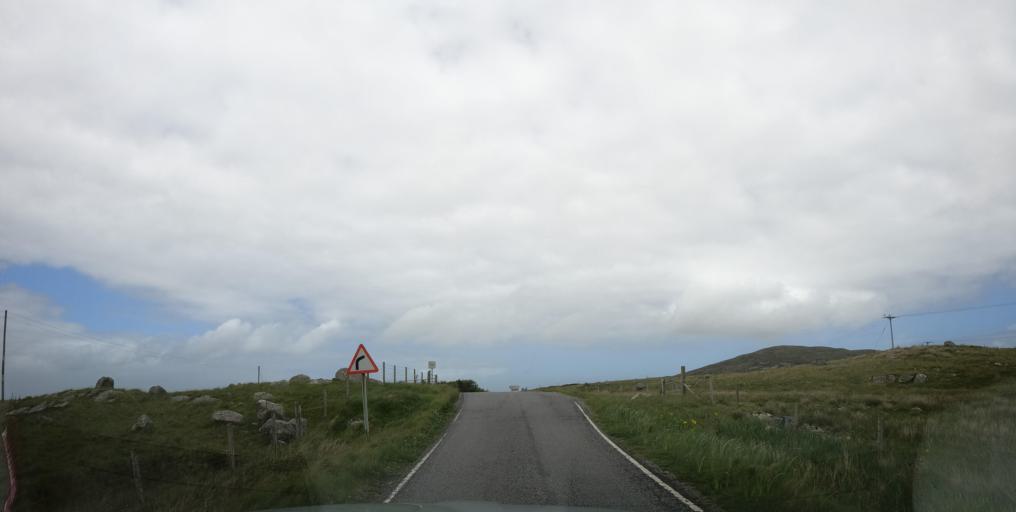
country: GB
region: Scotland
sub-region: Eilean Siar
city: Isle of South Uist
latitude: 57.2890
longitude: -7.3668
